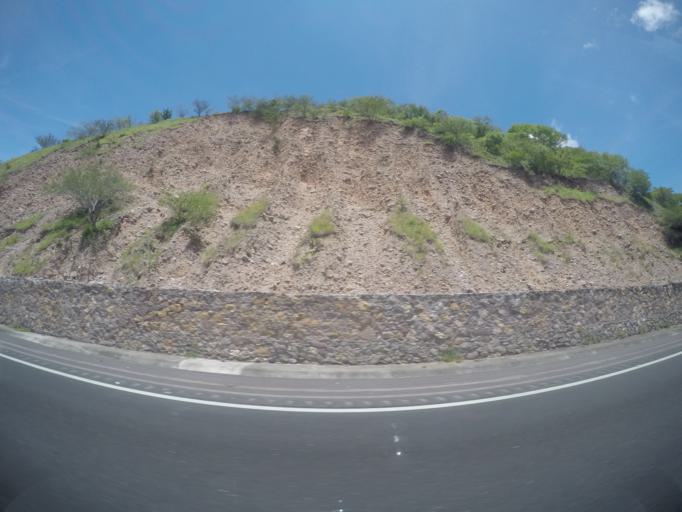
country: MX
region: Morelos
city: Tilzapotla
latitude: 18.4618
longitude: -99.1709
